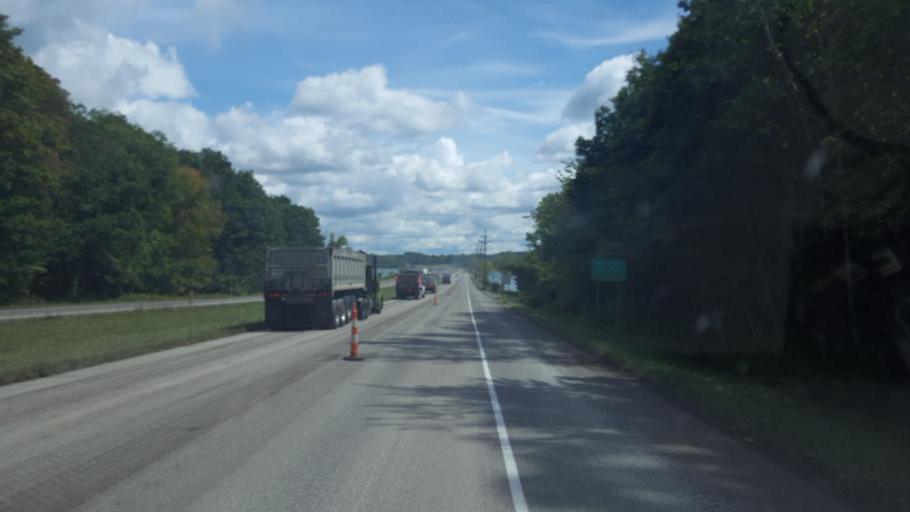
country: US
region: Ohio
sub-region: Portage County
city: Hiram
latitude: 41.3836
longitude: -81.2086
